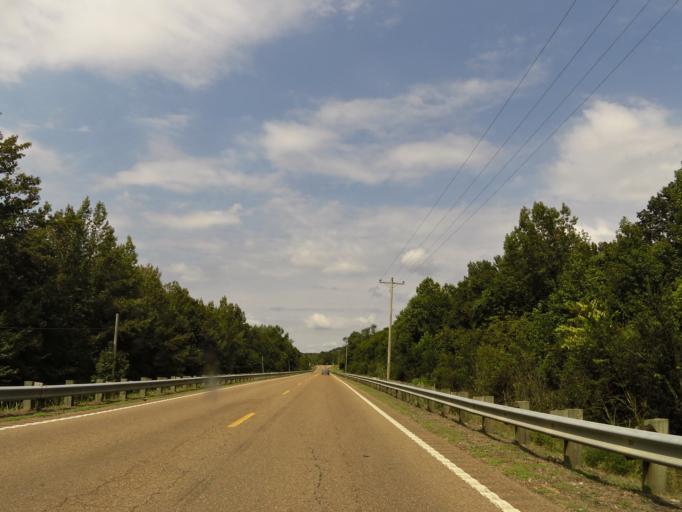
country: US
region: Tennessee
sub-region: Decatur County
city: Parsons
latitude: 35.6309
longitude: -88.0437
